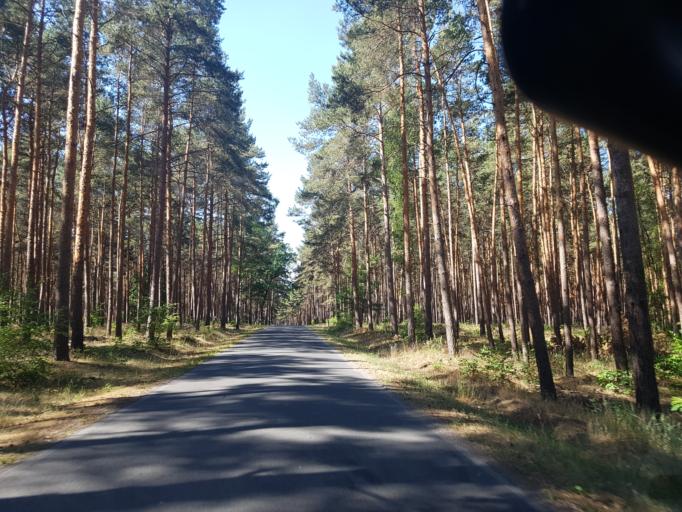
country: DE
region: Brandenburg
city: Treuenbrietzen
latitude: 52.0537
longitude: 12.8759
